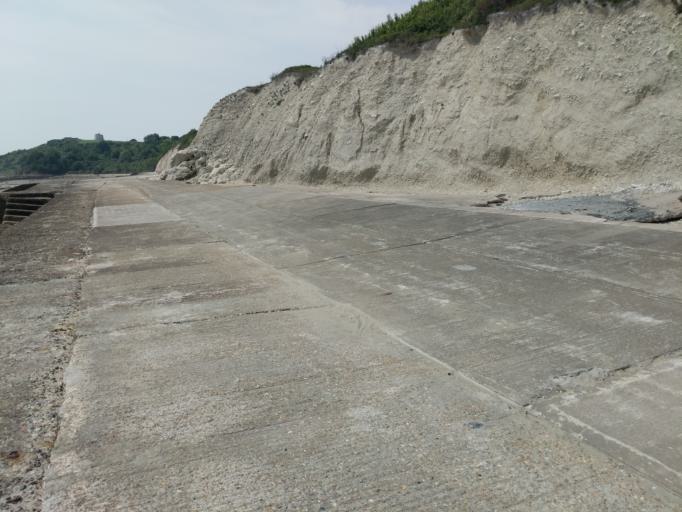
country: GB
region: England
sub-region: Kent
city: Folkestone
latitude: 51.0922
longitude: 1.2052
